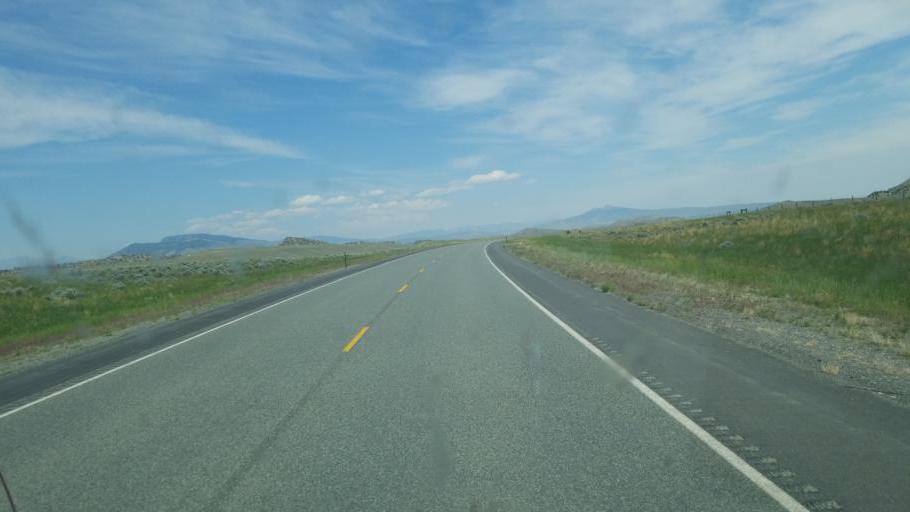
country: US
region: Wyoming
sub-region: Park County
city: Cody
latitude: 44.4053
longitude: -109.0043
